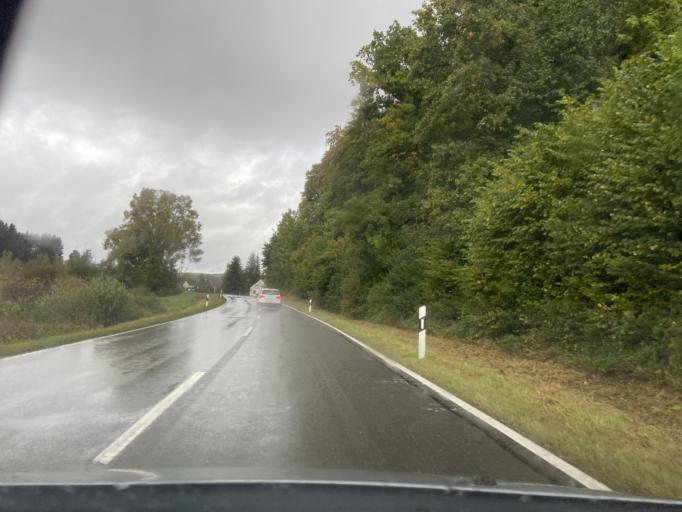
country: DE
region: Baden-Wuerttemberg
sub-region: Tuebingen Region
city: Bingen
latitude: 48.0989
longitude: 9.2868
